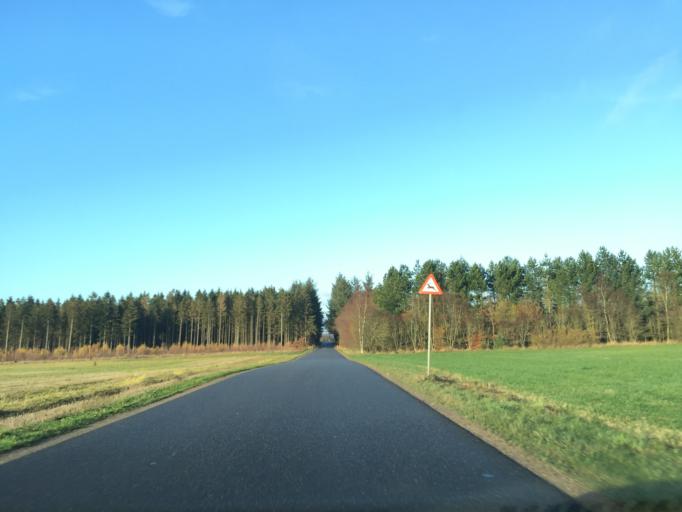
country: DK
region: Central Jutland
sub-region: Silkeborg Kommune
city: Svejbaek
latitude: 56.2242
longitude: 9.6821
